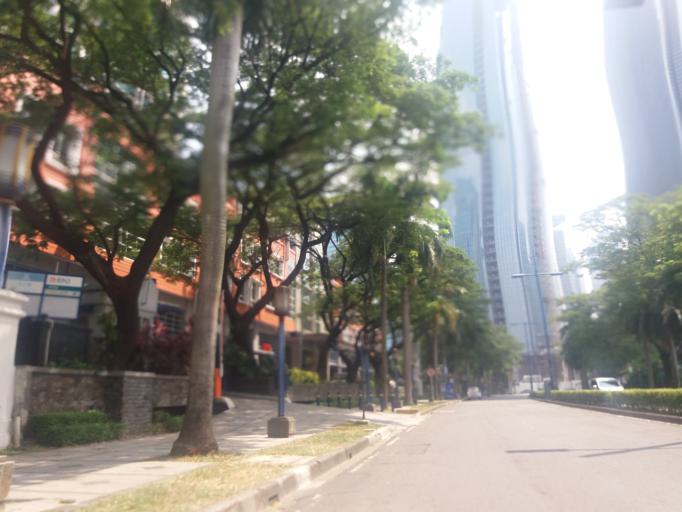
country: ID
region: Jakarta Raya
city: Jakarta
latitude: -6.2314
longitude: 106.8283
